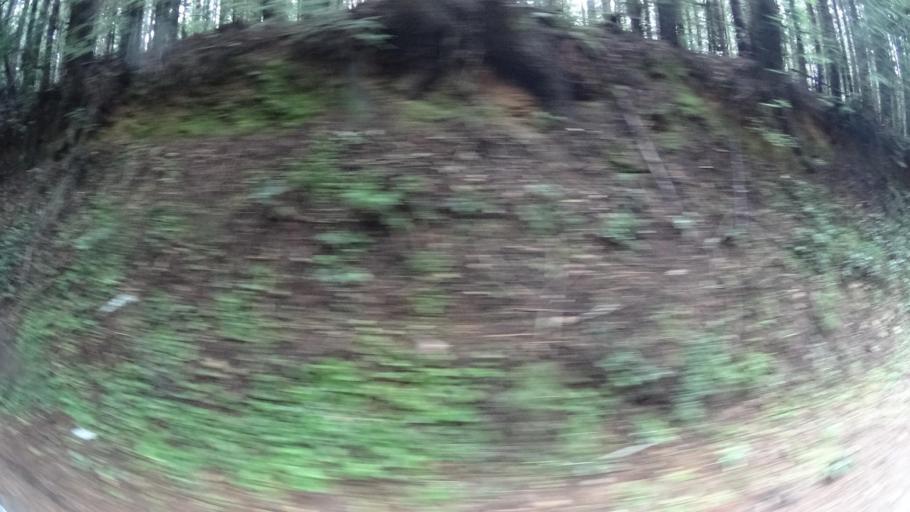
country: US
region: California
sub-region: Humboldt County
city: Westhaven-Moonstone
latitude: 41.2413
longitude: -123.9821
